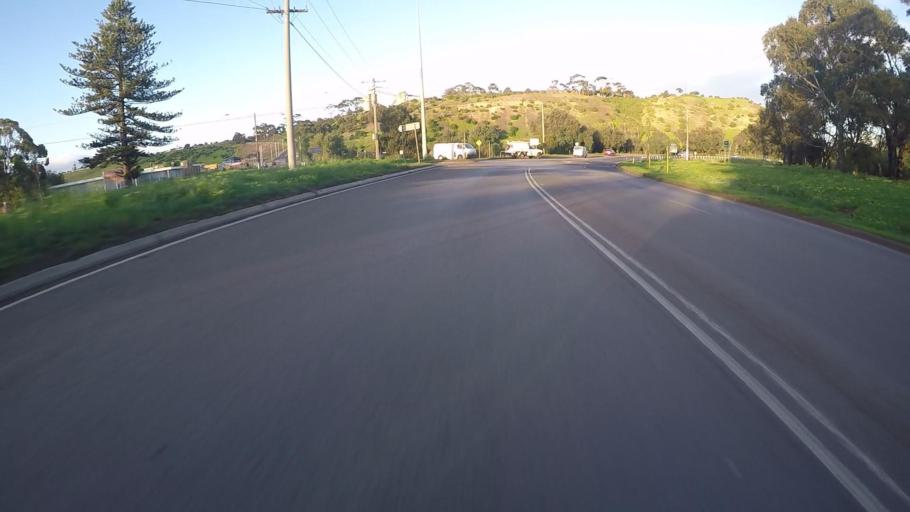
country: AU
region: Victoria
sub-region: Greater Geelong
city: Hamlyn Heights
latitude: -38.1413
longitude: 144.3110
